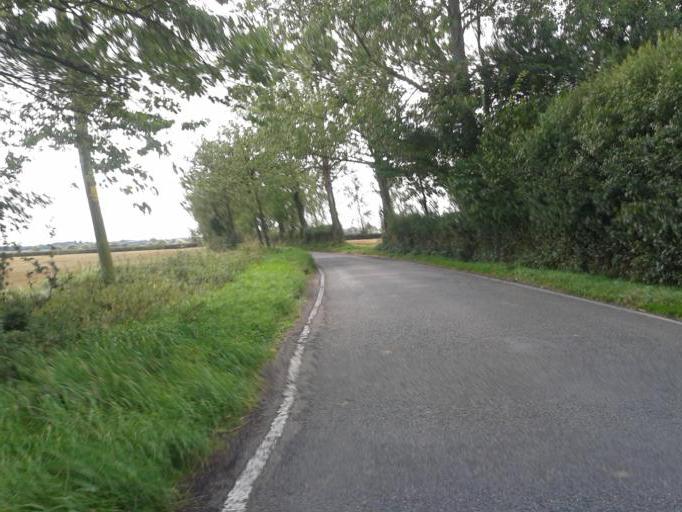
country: GB
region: England
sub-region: Cambridgeshire
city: Duxford
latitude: 52.0035
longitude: 0.1165
